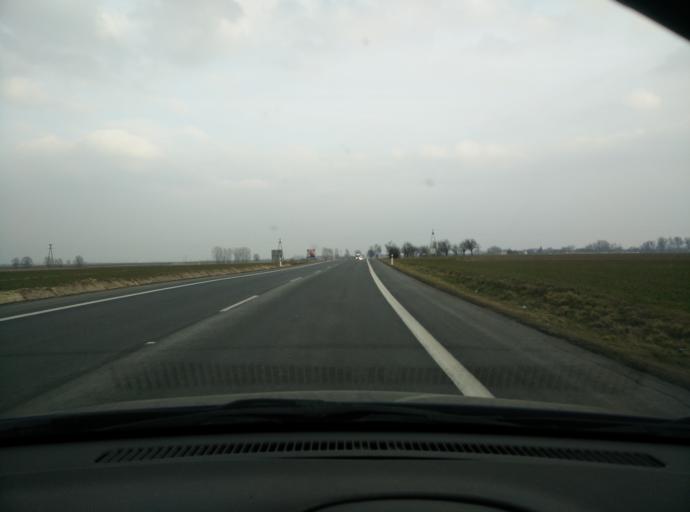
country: PL
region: Greater Poland Voivodeship
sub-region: Powiat poznanski
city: Kornik
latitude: 52.2419
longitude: 17.1405
